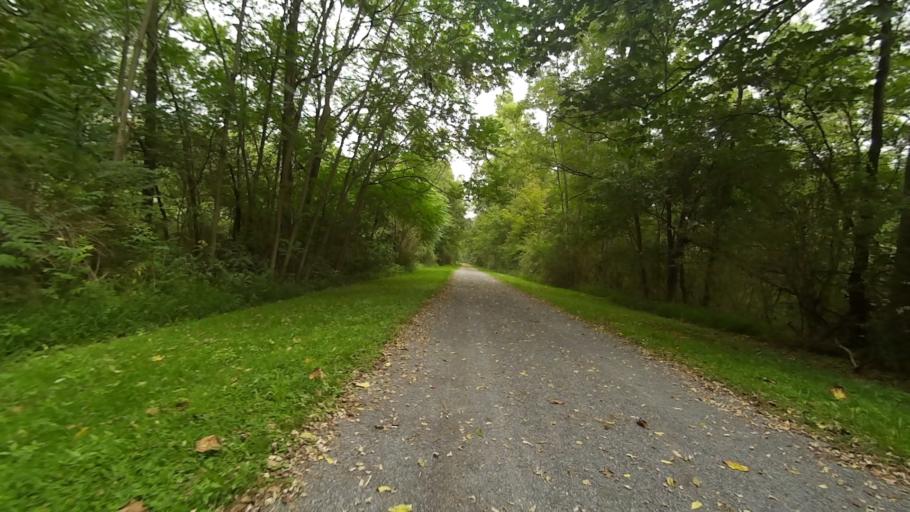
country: US
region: Pennsylvania
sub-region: Blair County
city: Williamsburg
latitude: 40.5337
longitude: -78.1657
